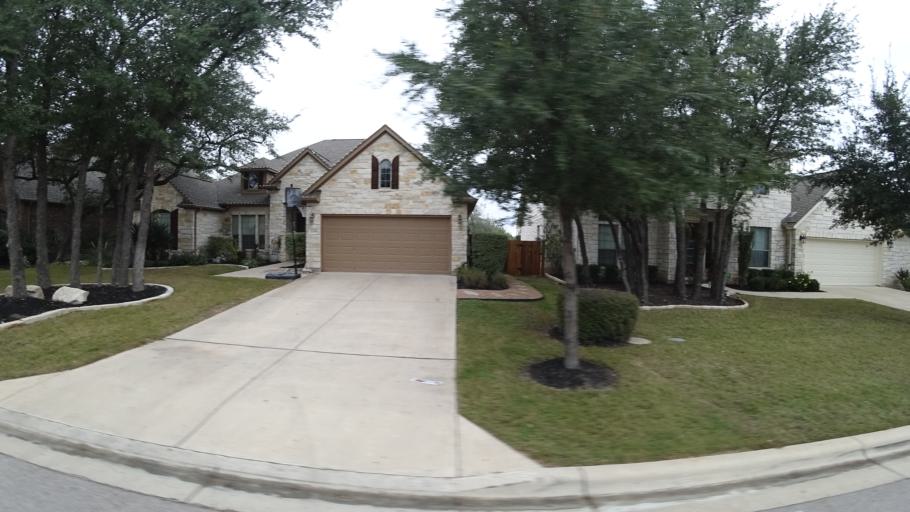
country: US
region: Texas
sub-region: Travis County
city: Bee Cave
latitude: 30.3445
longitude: -97.9084
